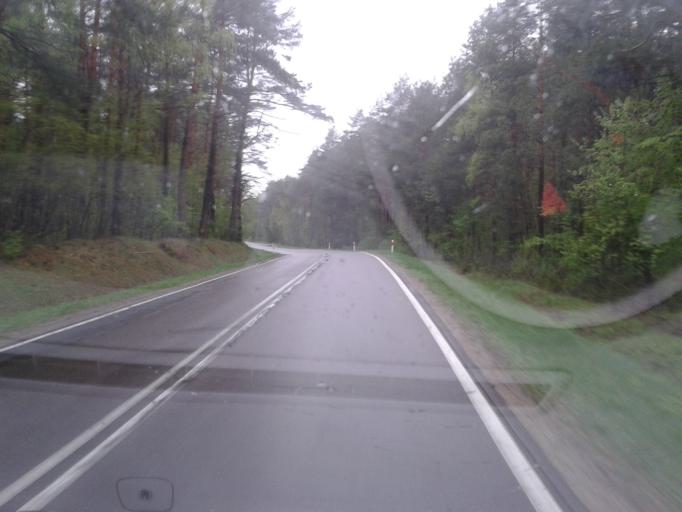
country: PL
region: Subcarpathian Voivodeship
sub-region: Powiat lubaczowski
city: Narol
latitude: 50.3701
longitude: 23.3636
